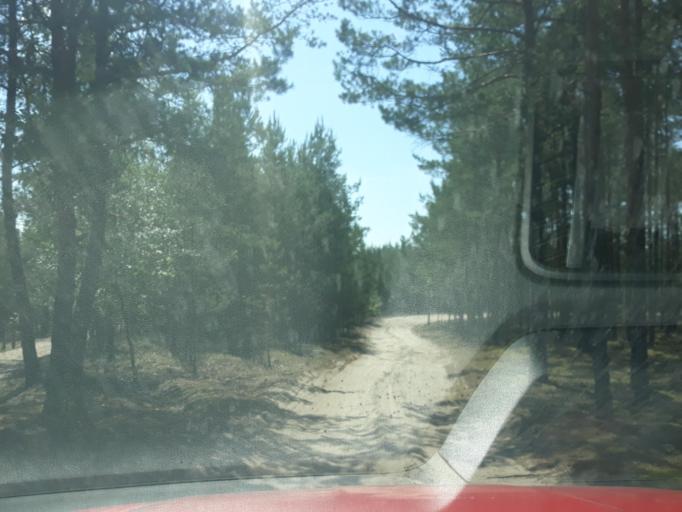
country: PL
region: Pomeranian Voivodeship
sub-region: Powiat chojnicki
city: Chojnice
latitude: 53.8686
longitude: 17.5431
